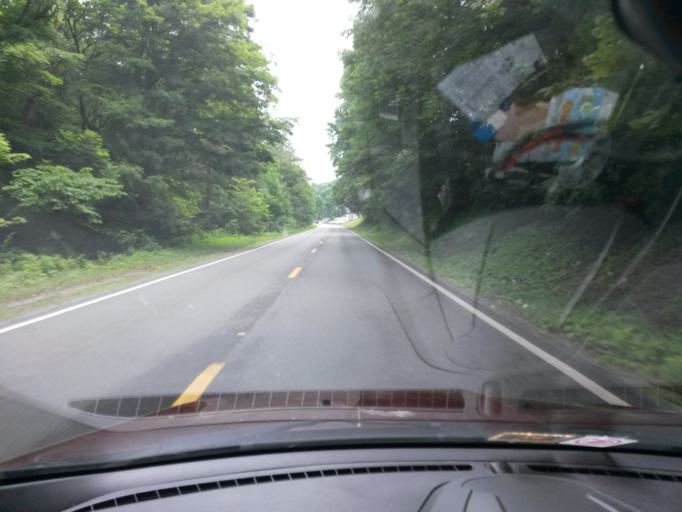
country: US
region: West Virginia
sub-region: Mercer County
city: Bluefield
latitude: 37.2796
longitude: -81.1855
